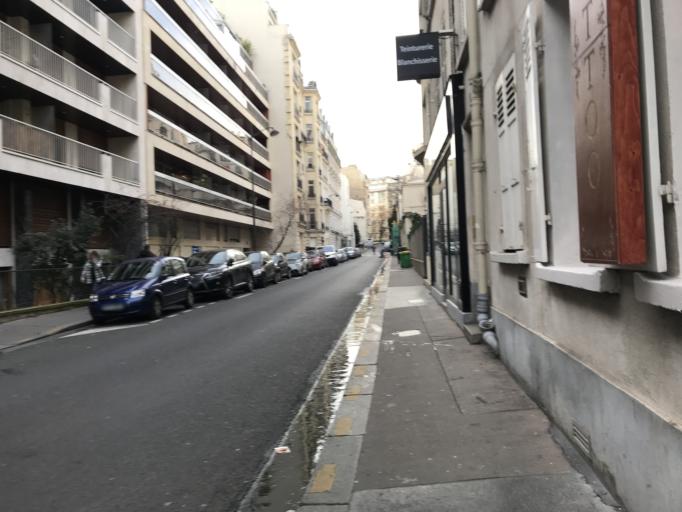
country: FR
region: Ile-de-France
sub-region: Departement des Hauts-de-Seine
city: Boulogne-Billancourt
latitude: 48.8553
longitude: 2.2677
